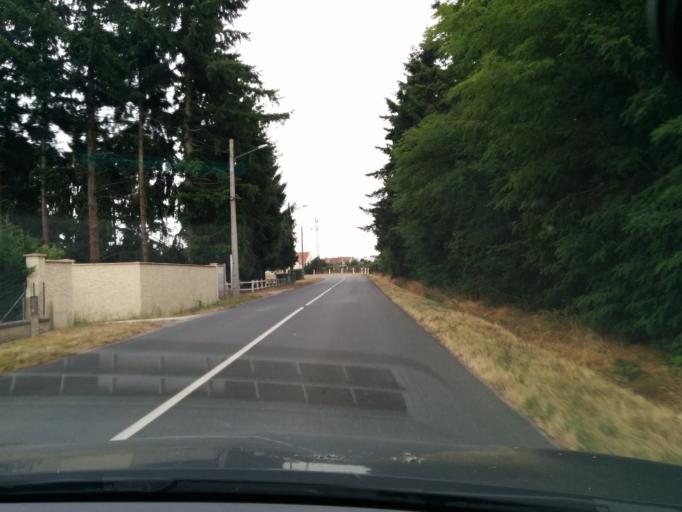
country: FR
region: Centre
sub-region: Departement du Loiret
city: Chateauneuf-sur-Loire
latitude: 47.8726
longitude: 2.2017
